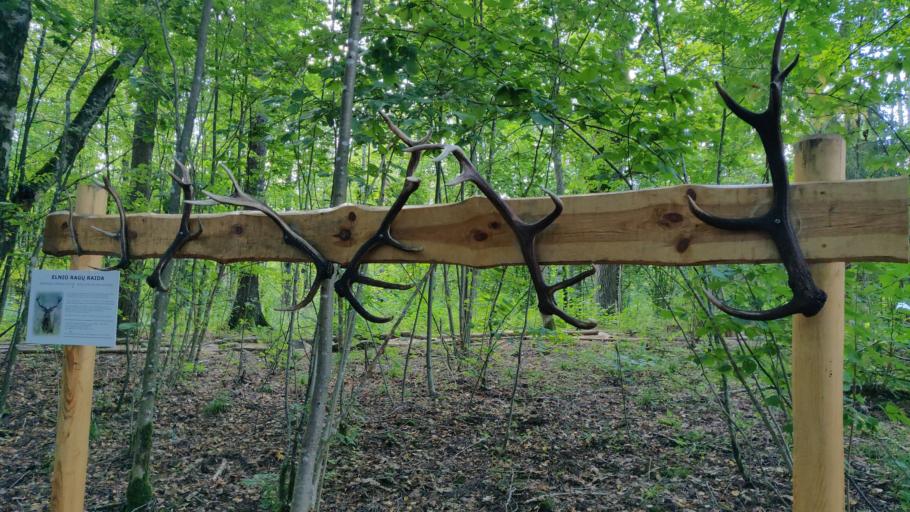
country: LT
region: Utenos apskritis
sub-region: Anyksciai
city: Anyksciai
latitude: 55.4743
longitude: 25.0530
